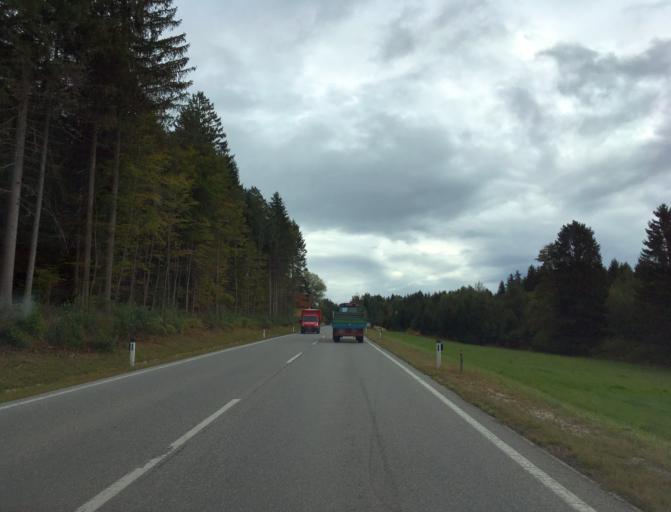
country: AT
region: Lower Austria
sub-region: Politischer Bezirk Neunkirchen
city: Thomasberg
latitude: 47.5441
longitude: 16.1506
